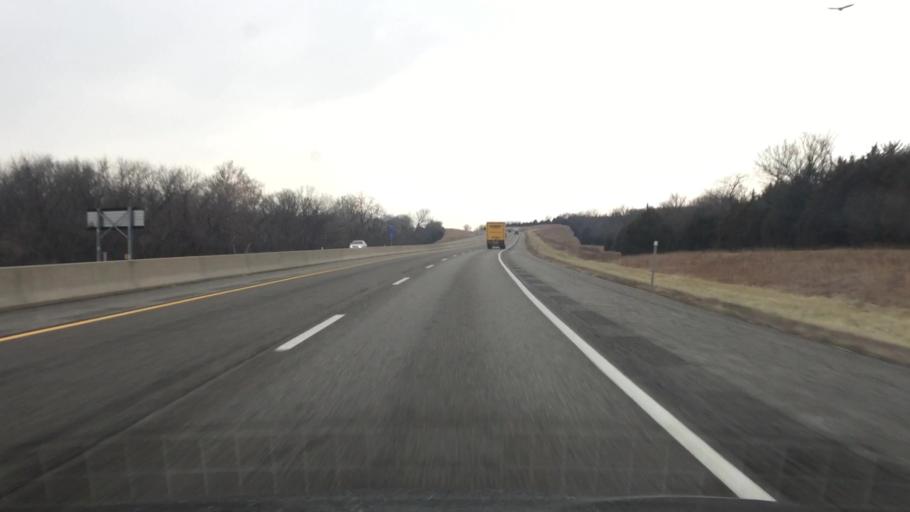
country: US
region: Kansas
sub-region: Shawnee County
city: Topeka
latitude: 38.9622
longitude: -95.7230
